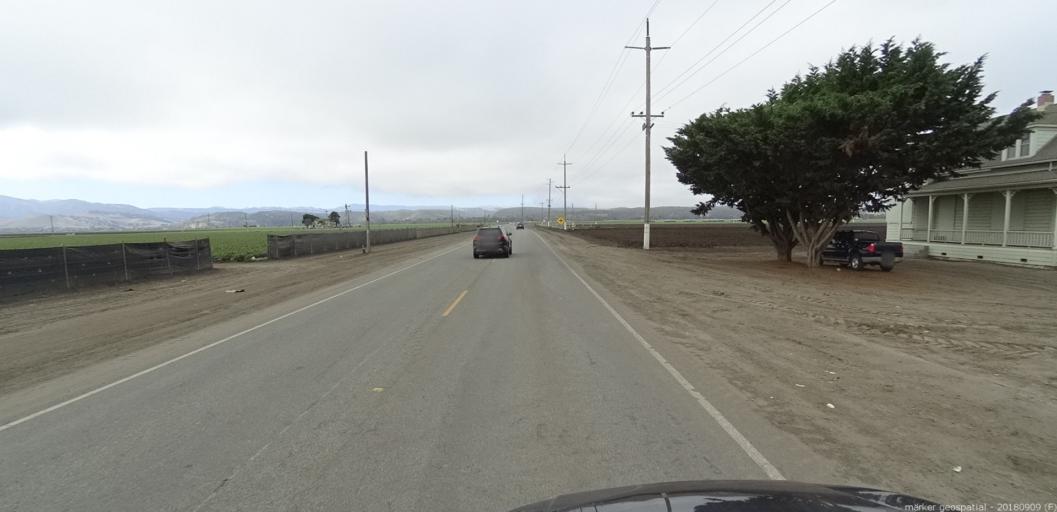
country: US
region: California
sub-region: Monterey County
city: Salinas
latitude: 36.6608
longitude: -121.6903
